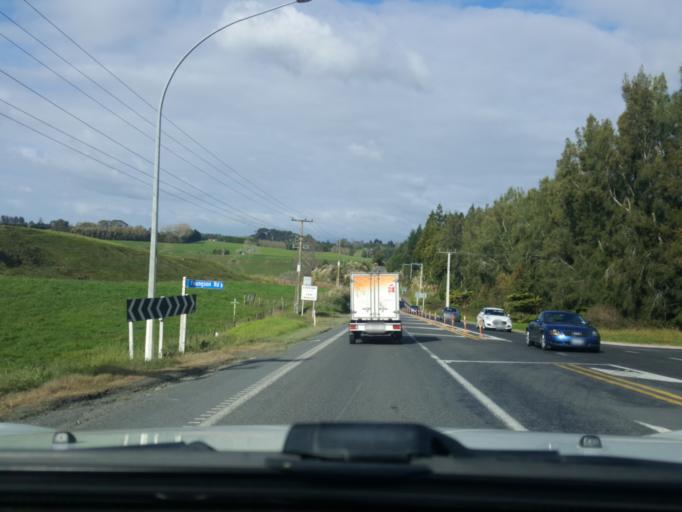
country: NZ
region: Bay of Plenty
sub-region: Western Bay of Plenty District
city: Katikati
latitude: -37.6653
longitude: 176.0155
